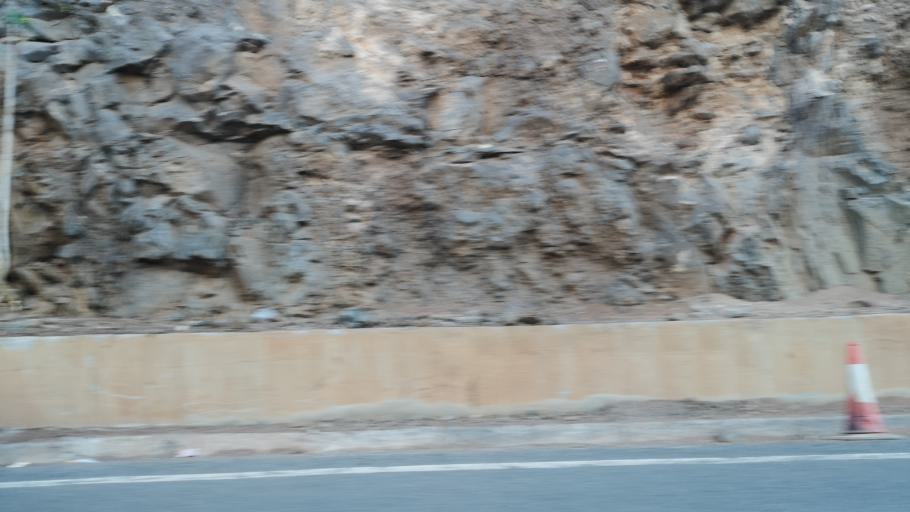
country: ES
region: Canary Islands
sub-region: Provincia de Santa Cruz de Tenerife
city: Alajero
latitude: 28.0336
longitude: -17.2019
